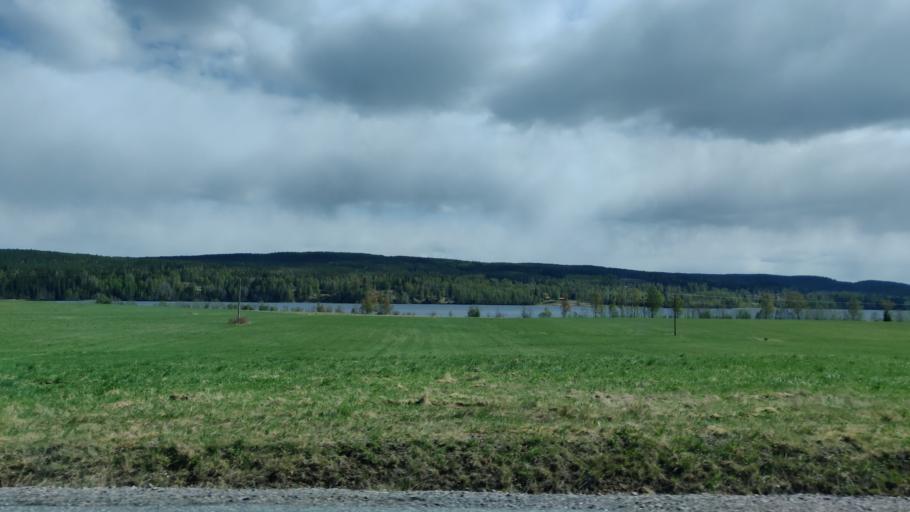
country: SE
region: Vaermland
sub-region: Hagfors Kommun
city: Hagfors
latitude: 59.8631
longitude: 13.7072
